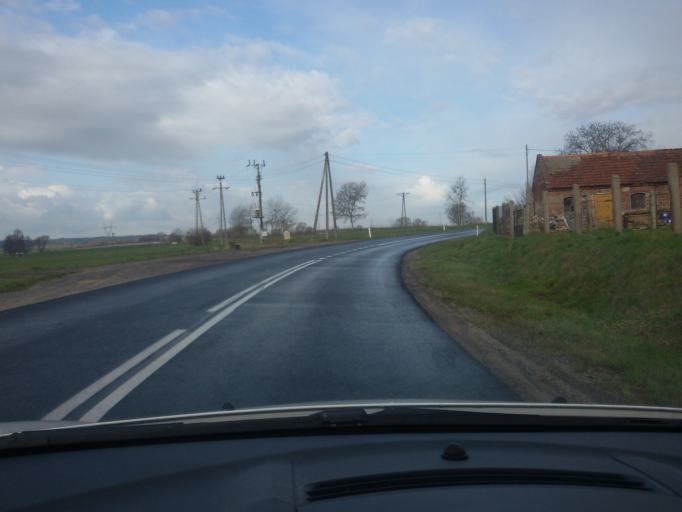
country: PL
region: Lower Silesian Voivodeship
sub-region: Powiat polkowicki
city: Gaworzyce
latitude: 51.6885
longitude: 15.9234
